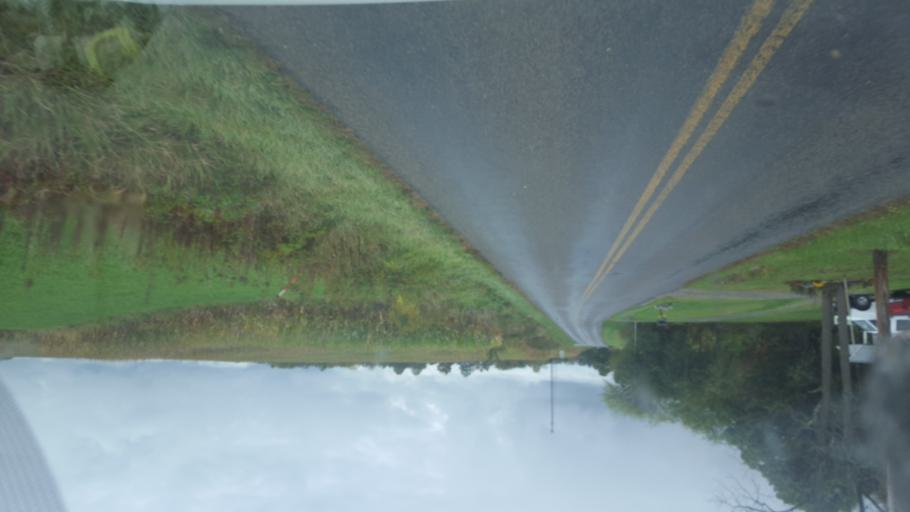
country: US
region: Ohio
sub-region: Holmes County
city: Millersburg
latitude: 40.5653
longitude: -82.0045
